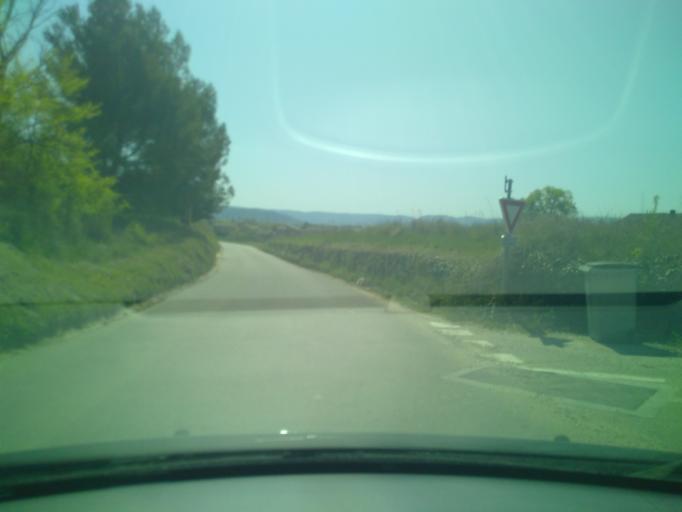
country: FR
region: Provence-Alpes-Cote d'Azur
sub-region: Departement du Vaucluse
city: Mazan
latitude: 44.0626
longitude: 5.1178
